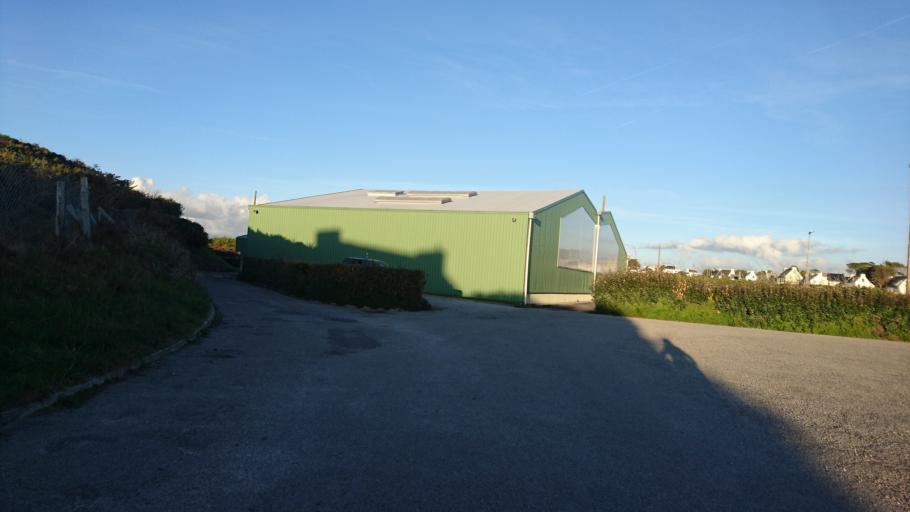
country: FR
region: Brittany
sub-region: Departement du Finistere
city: Lampaul-Plouarzel
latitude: 48.4483
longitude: -4.7765
